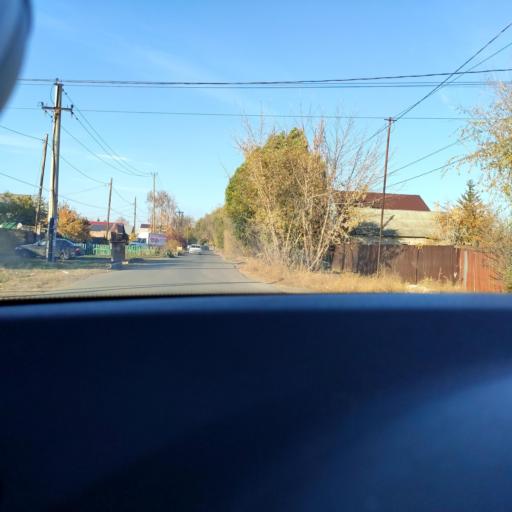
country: RU
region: Samara
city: Petra-Dubrava
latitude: 53.2467
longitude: 50.3280
